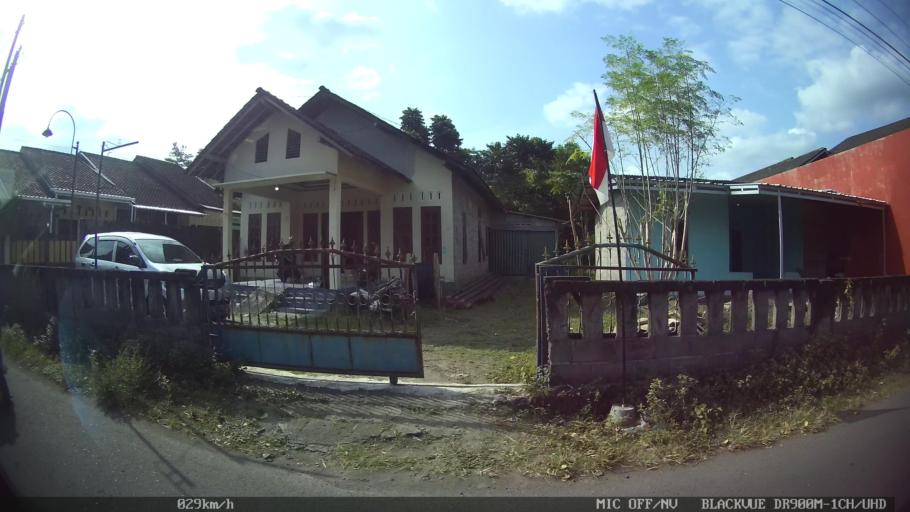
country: ID
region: Daerah Istimewa Yogyakarta
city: Depok
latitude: -7.7367
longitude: 110.4503
